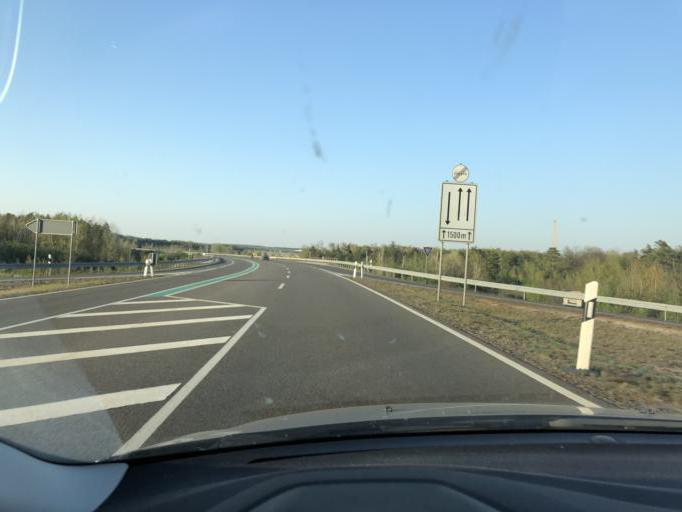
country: DE
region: Brandenburg
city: Senftenberg
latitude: 51.5006
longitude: 13.9559
